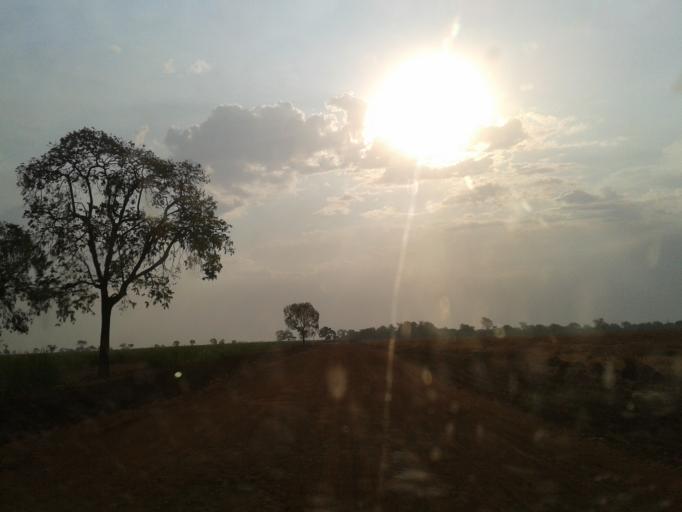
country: BR
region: Minas Gerais
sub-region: Capinopolis
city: Capinopolis
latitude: -18.7563
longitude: -49.7023
